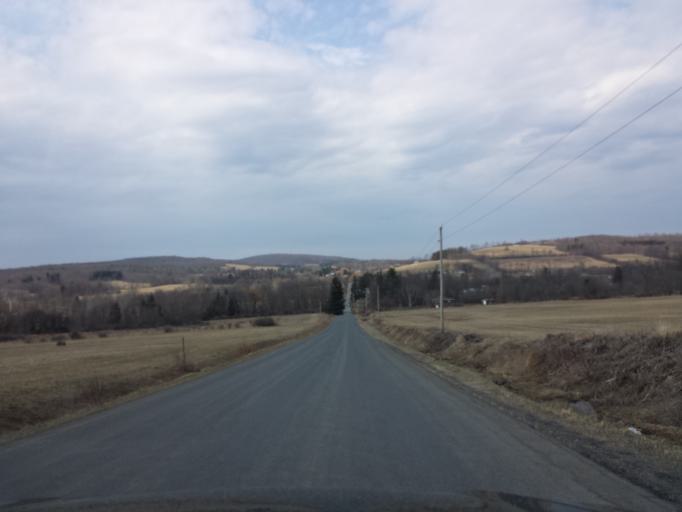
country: US
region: New York
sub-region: Tompkins County
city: Dryden
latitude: 42.3876
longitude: -76.3502
